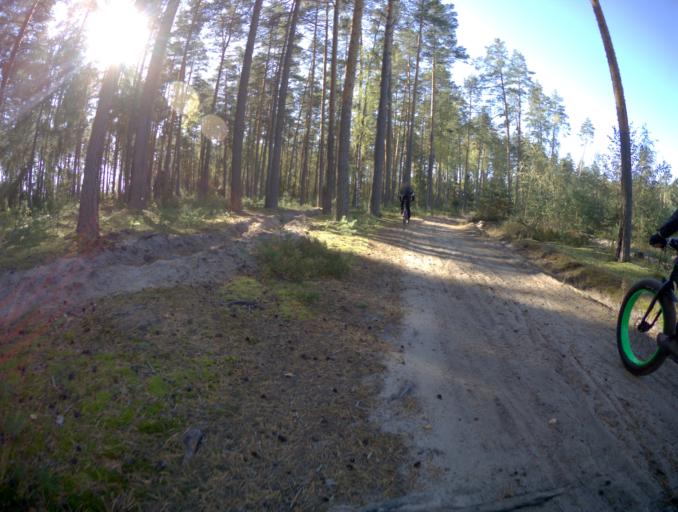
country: RU
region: Vladimir
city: Sobinka
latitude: 55.9625
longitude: 40.0056
